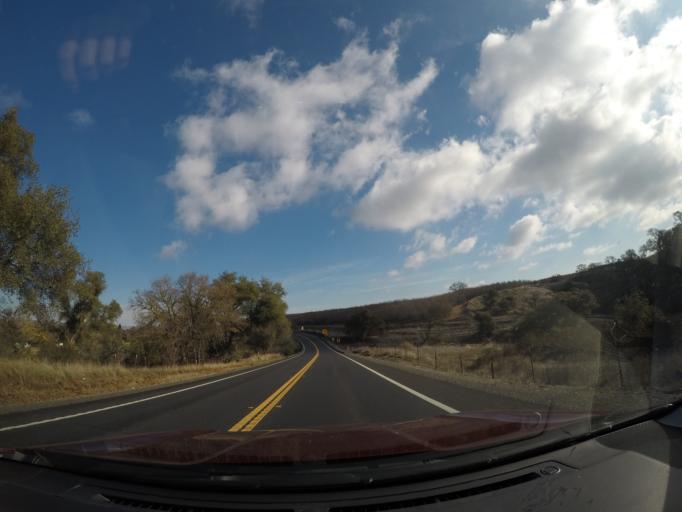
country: US
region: California
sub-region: Stanislaus County
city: East Oakdale
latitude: 37.7874
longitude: -120.7308
